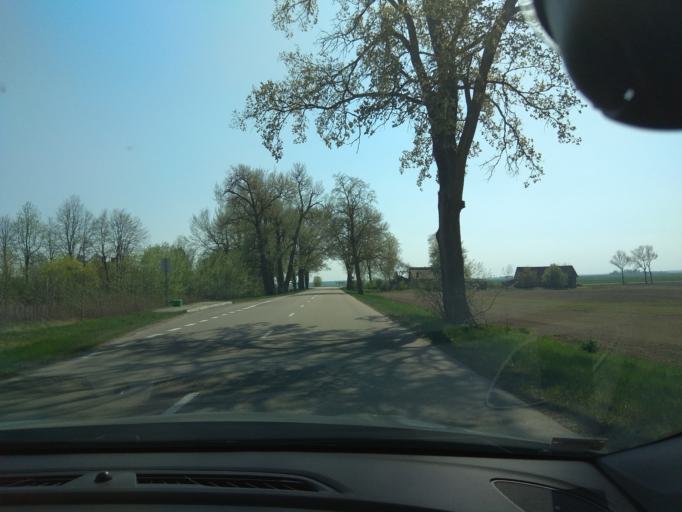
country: LT
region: Panevezys
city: Pasvalys
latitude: 55.9462
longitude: 24.2130
